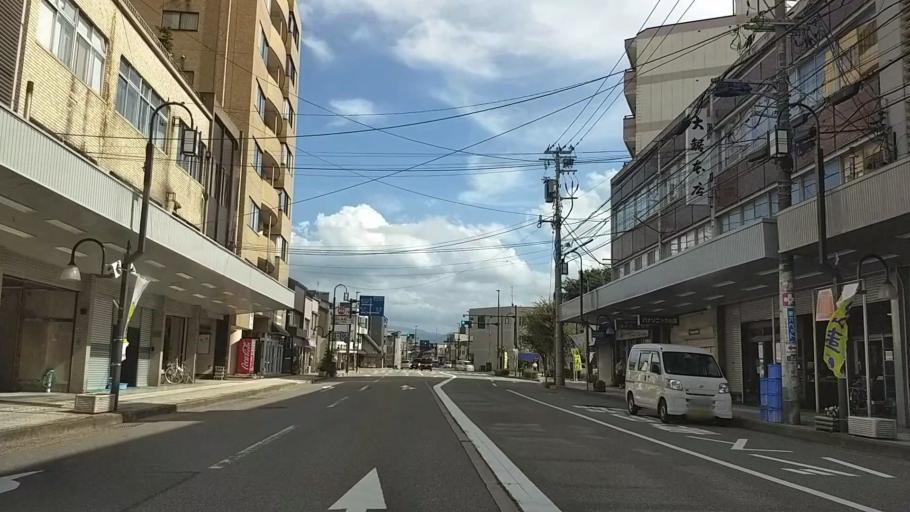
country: JP
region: Ishikawa
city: Nonoichi
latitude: 36.5536
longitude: 136.6726
